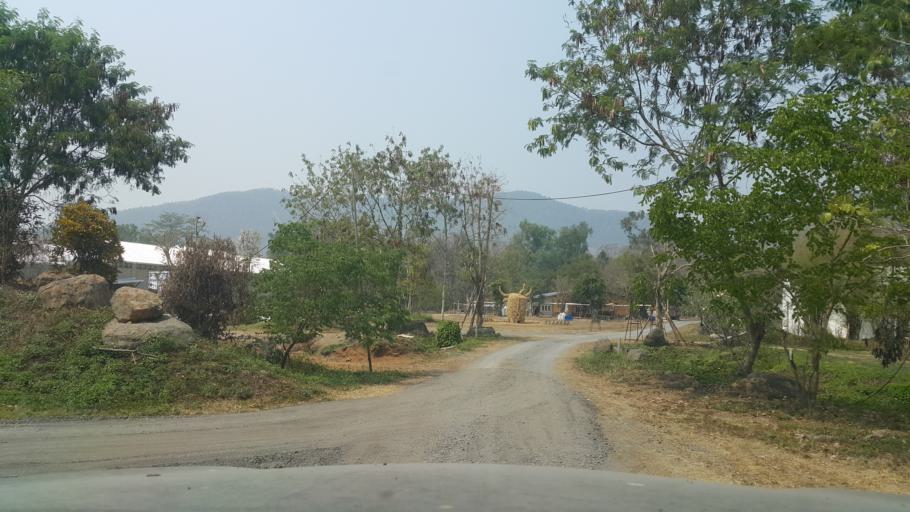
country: TH
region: Chiang Mai
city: Mae On
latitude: 18.7408
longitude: 99.2159
